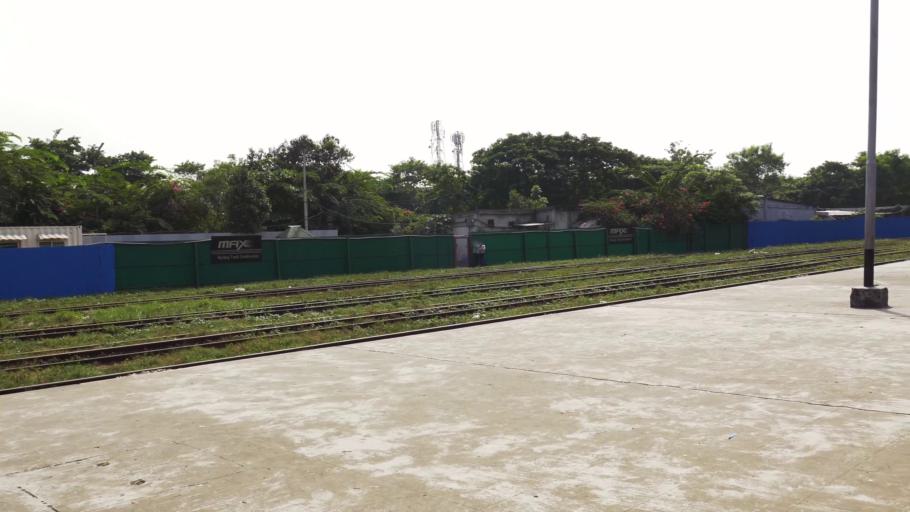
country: BD
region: Dhaka
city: Tungi
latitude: 23.8545
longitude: 90.4066
